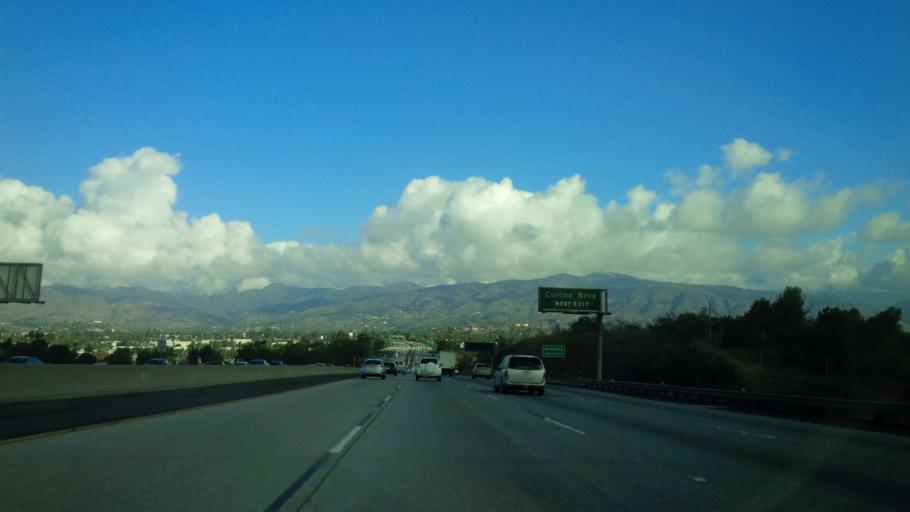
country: US
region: California
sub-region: Los Angeles County
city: San Dimas
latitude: 34.0896
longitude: -117.8194
